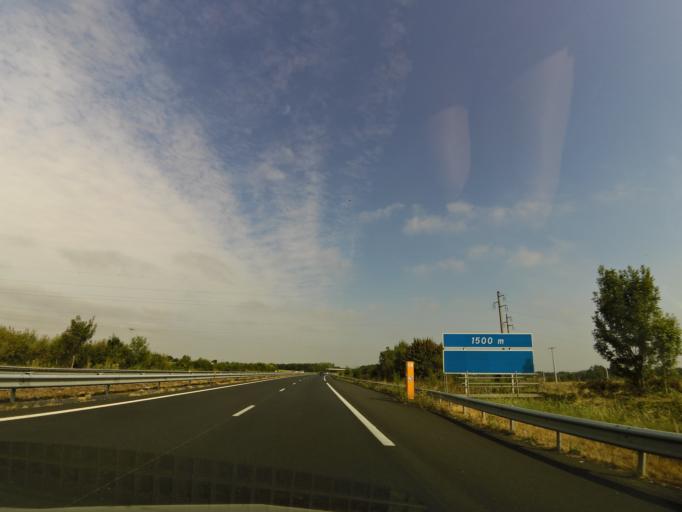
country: FR
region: Pays de la Loire
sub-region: Departement de la Vendee
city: Chauche
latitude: 46.8560
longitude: -1.2793
